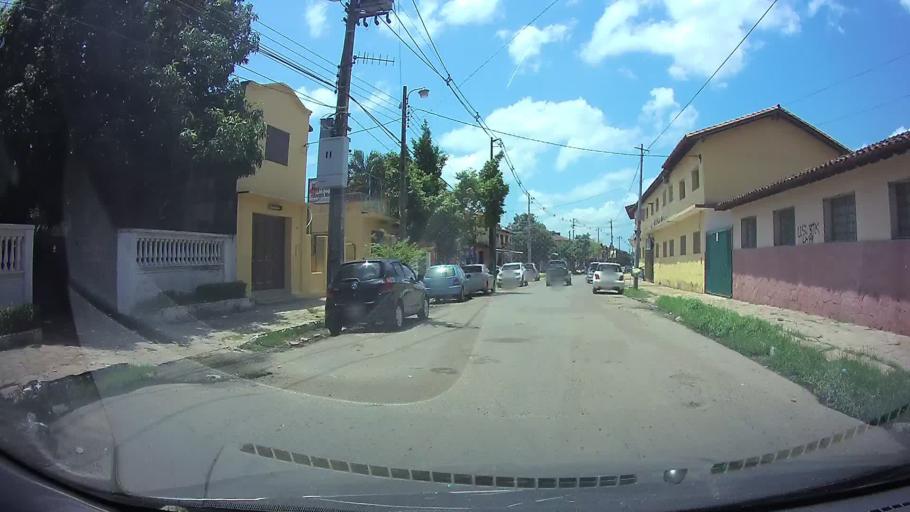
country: PY
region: Central
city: Fernando de la Mora
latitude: -25.2995
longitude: -57.5492
